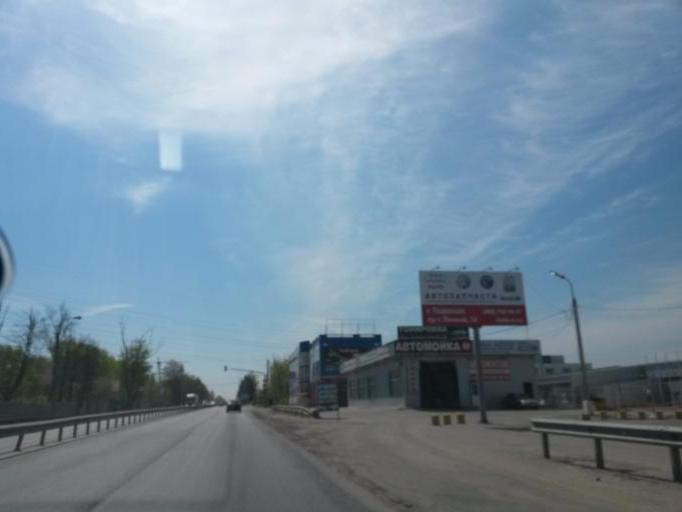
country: RU
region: Moskovskaya
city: Shcherbinka
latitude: 55.4893
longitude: 37.5678
